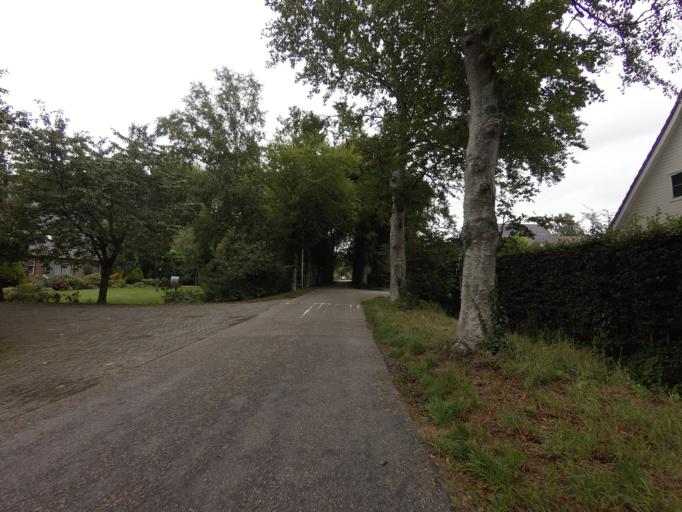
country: NL
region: Friesland
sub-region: Gemeente Weststellingwerf
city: Steggerda
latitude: 52.8859
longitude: 6.0878
